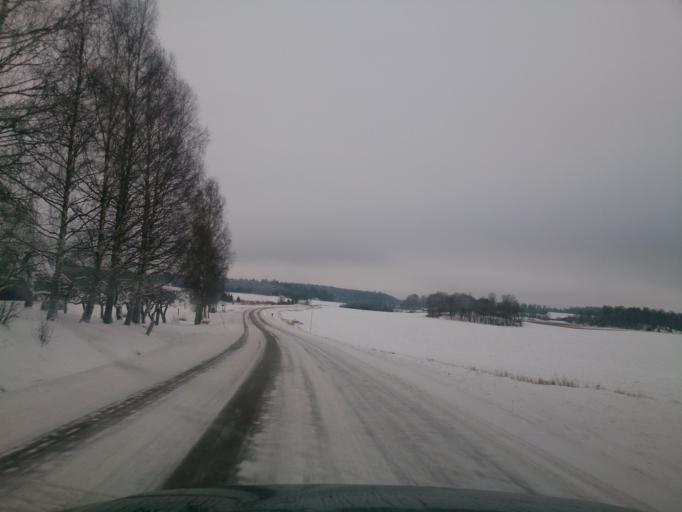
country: SE
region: OEstergoetland
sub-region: Linkopings Kommun
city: Linghem
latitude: 58.4552
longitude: 15.8849
